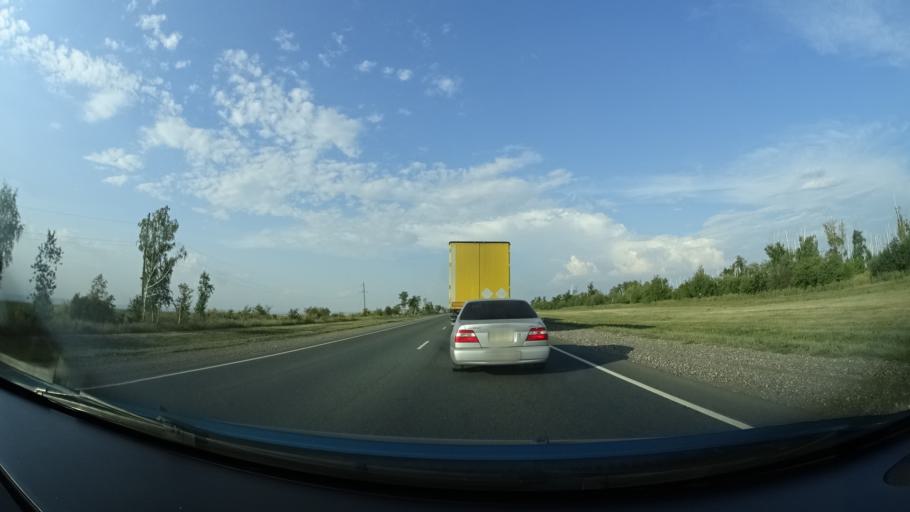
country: RU
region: Samara
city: Krasnyy Yar
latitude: 53.6711
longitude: 50.7670
